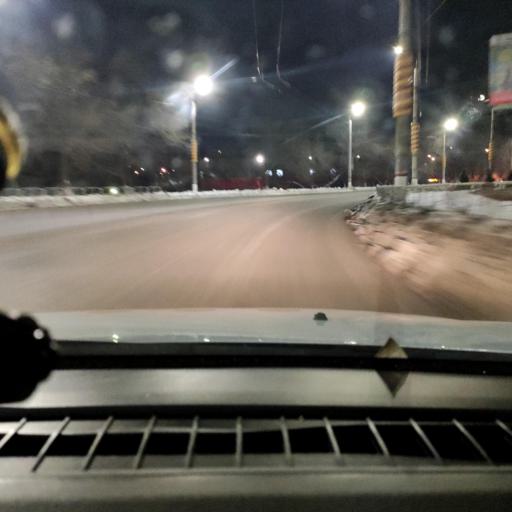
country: RU
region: Samara
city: Novokuybyshevsk
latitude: 53.0865
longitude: 49.9541
